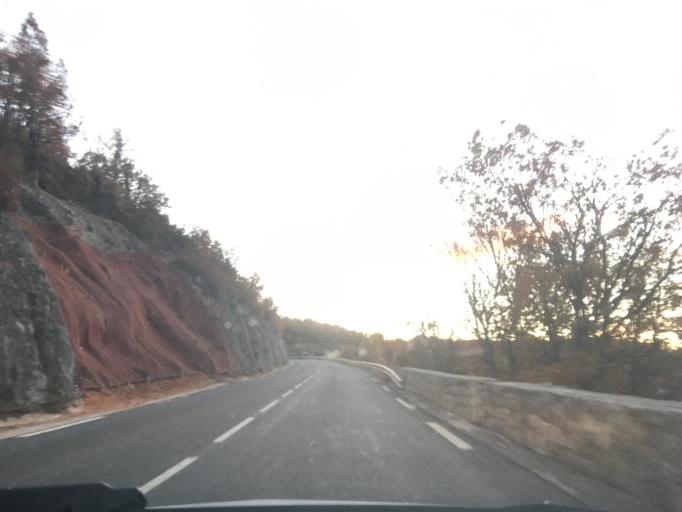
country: FR
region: Provence-Alpes-Cote d'Azur
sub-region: Departement du Var
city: Montferrat
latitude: 43.6703
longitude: 6.4928
